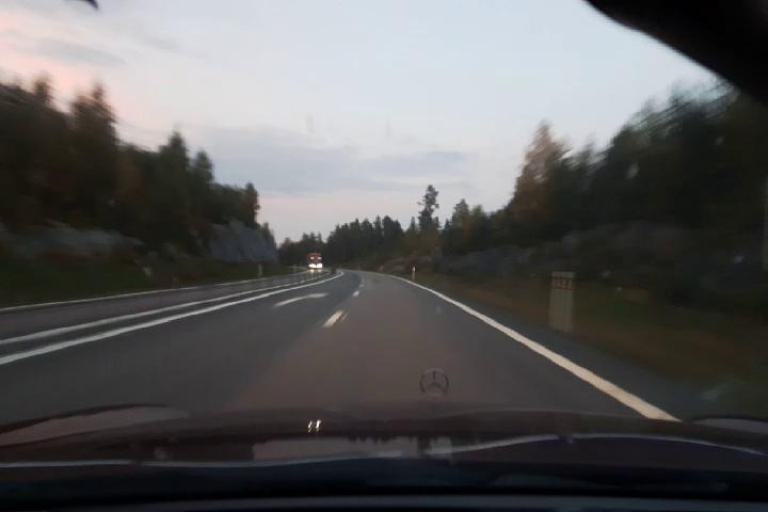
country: SE
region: Vaesternorrland
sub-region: Kramfors Kommun
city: Nordingra
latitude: 62.8837
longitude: 18.0852
